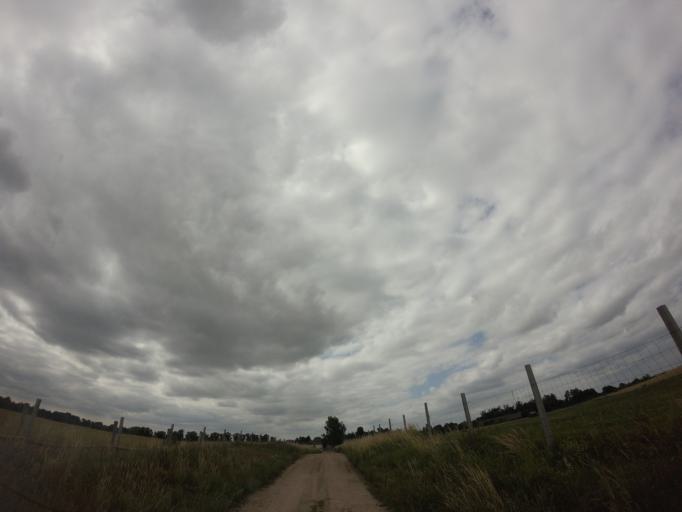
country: PL
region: Lubusz
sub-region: Powiat strzelecko-drezdenecki
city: Strzelce Krajenskie
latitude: 52.9084
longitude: 15.5994
